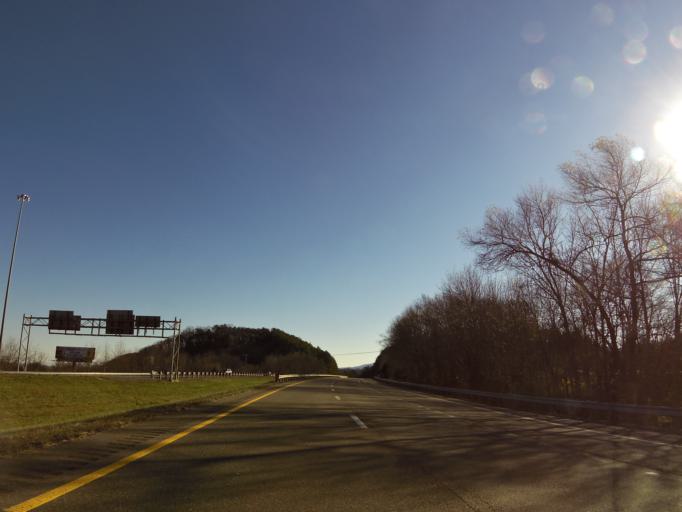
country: US
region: Tennessee
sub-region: Cocke County
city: Newport
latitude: 35.9685
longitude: -83.2515
